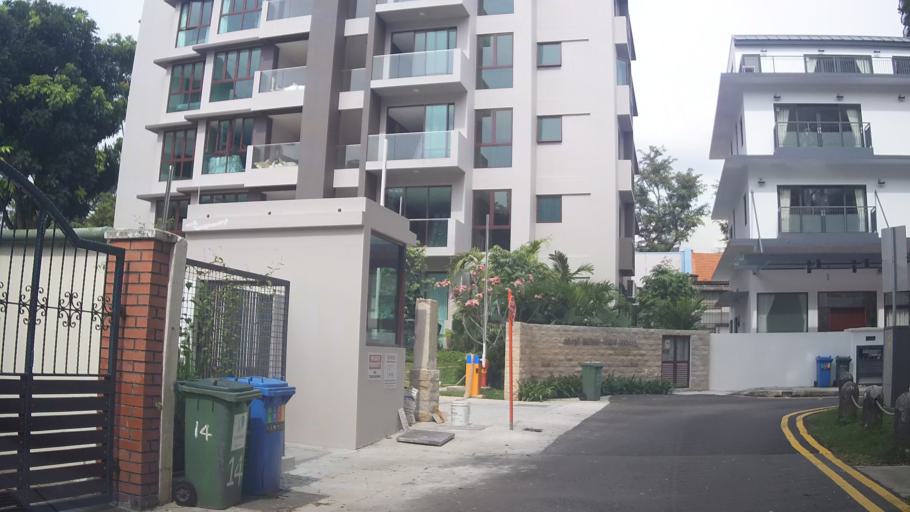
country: SG
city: Singapore
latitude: 1.3229
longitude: 103.8654
